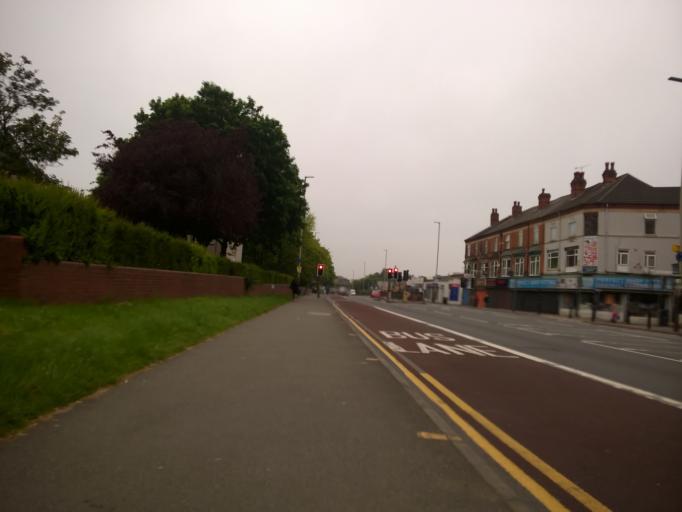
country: GB
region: England
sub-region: City of Leicester
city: Leicester
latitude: 52.6412
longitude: -1.1106
